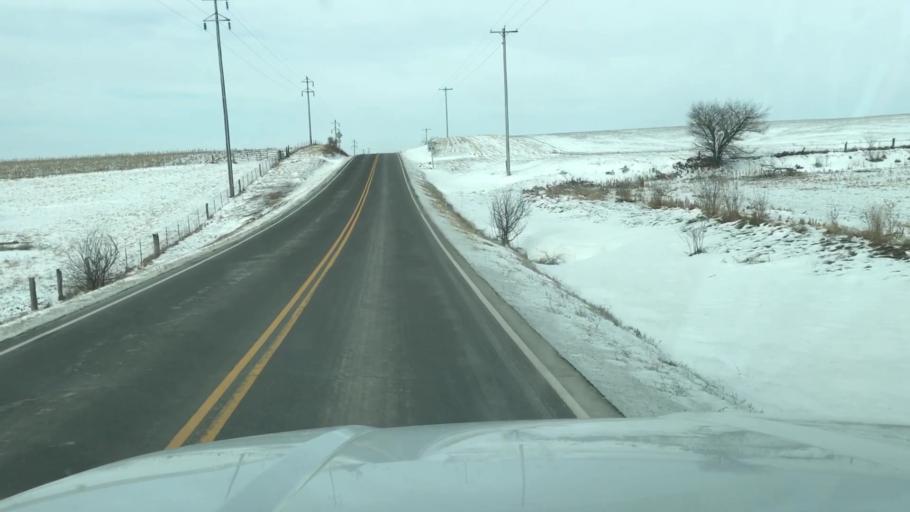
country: US
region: Missouri
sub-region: Holt County
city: Mound City
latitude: 40.1301
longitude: -95.0925
